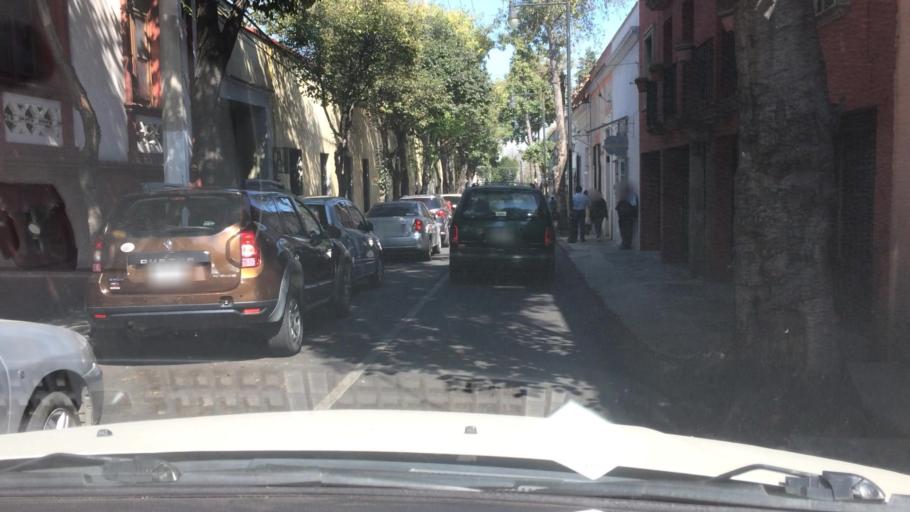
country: MX
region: Mexico City
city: Tlalpan
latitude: 19.2869
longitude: -99.1671
